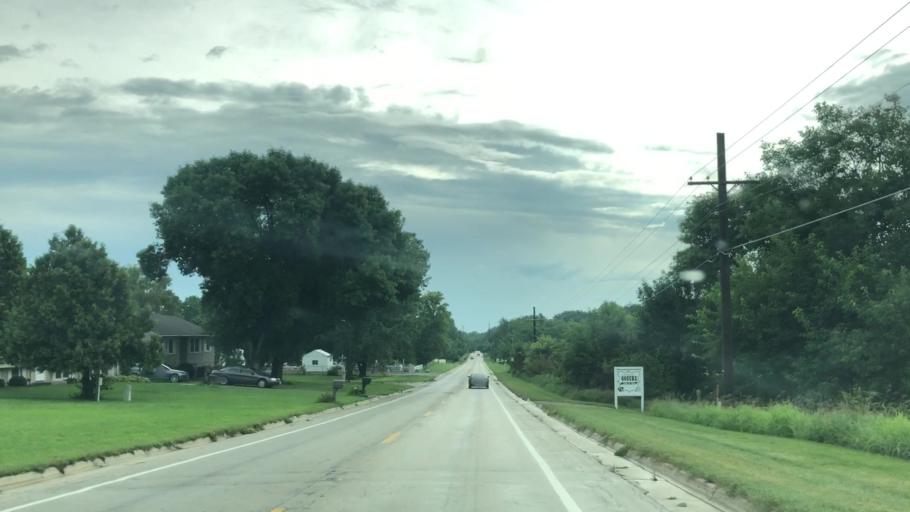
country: US
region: Iowa
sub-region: Marshall County
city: Marshalltown
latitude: 42.0490
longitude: -92.9535
